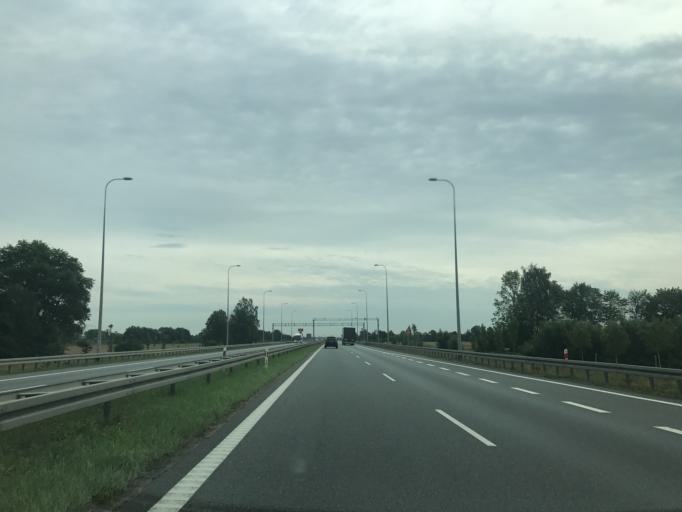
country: PL
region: Pomeranian Voivodeship
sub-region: Powiat gdanski
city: Suchy Dab
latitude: 54.3150
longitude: 18.7551
